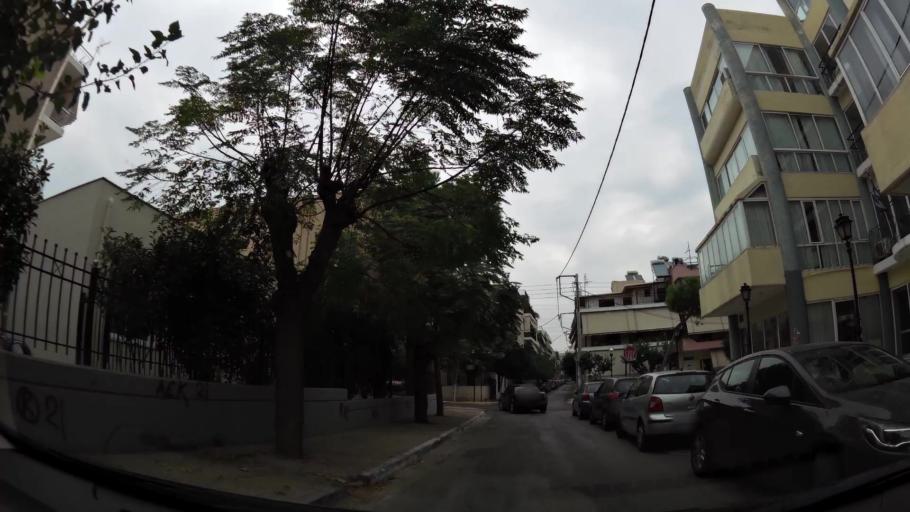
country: GR
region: Attica
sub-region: Nomarchia Athinas
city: Agia Varvara
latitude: 37.9851
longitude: 23.6647
